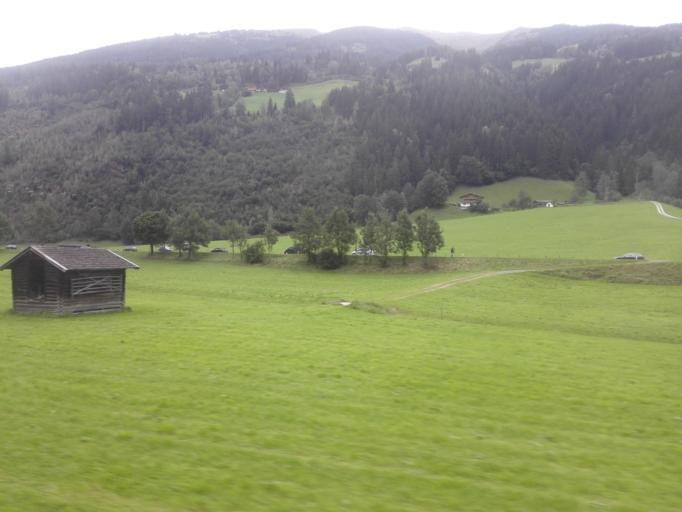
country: AT
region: Salzburg
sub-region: Politischer Bezirk Zell am See
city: Neukirchen am Grossvenediger
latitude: 47.2527
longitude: 12.2955
